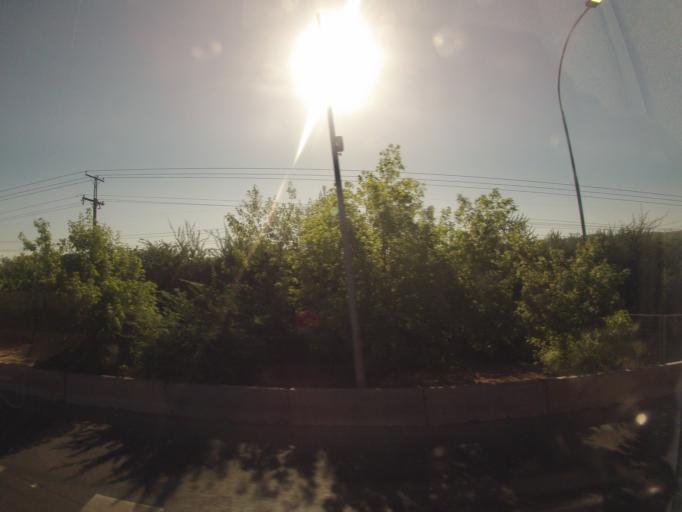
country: CL
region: Santiago Metropolitan
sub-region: Provincia de Maipo
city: San Bernardo
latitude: -33.6223
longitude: -70.7148
